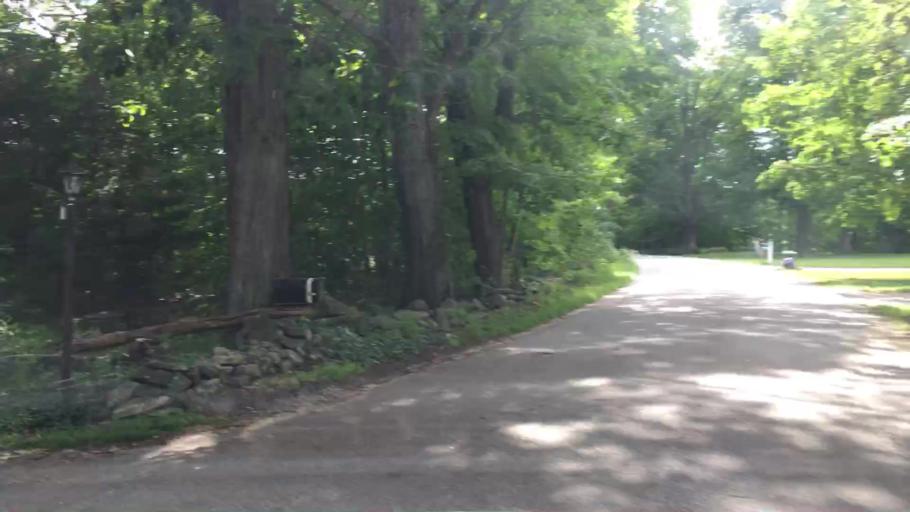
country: US
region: New Hampshire
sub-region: Strafford County
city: Madbury
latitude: 43.1627
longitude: -70.9259
